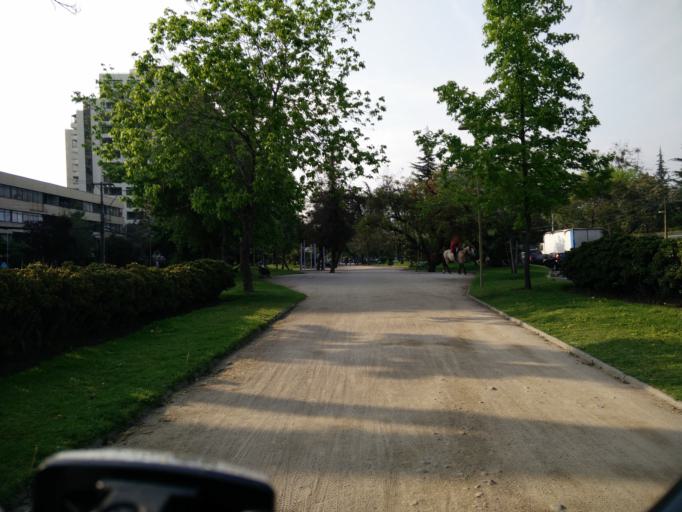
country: CL
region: Santiago Metropolitan
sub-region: Provincia de Santiago
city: Villa Presidente Frei, Nunoa, Santiago, Chile
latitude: -33.4121
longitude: -70.5857
